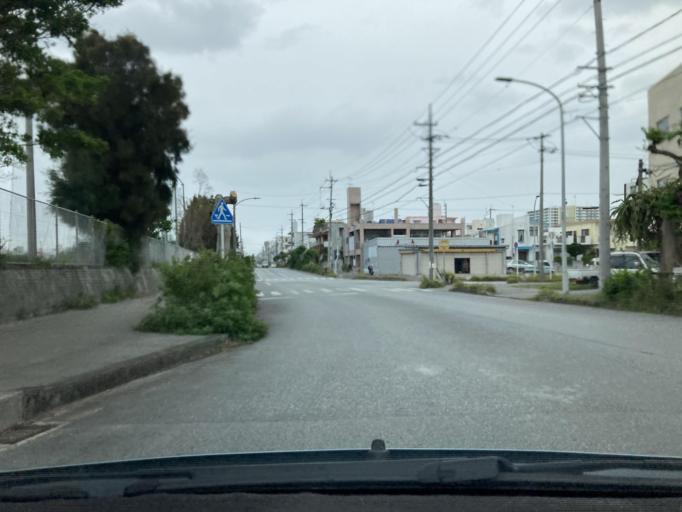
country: JP
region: Okinawa
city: Itoman
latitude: 26.1368
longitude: 127.6672
